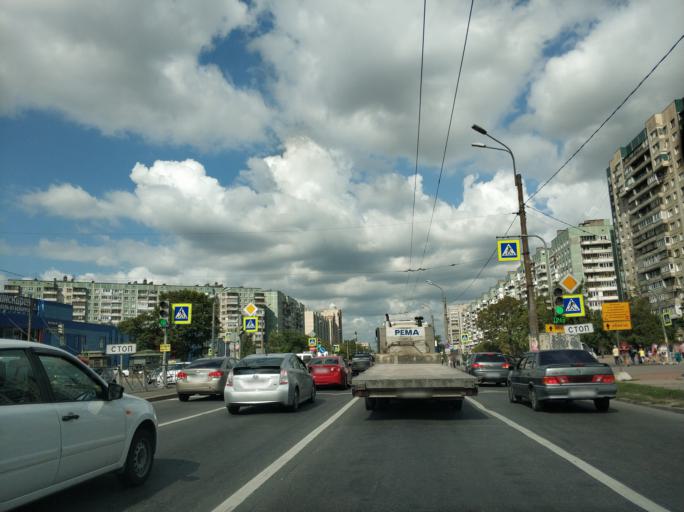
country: RU
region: St.-Petersburg
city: Krasnogvargeisky
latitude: 59.9510
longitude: 30.4722
